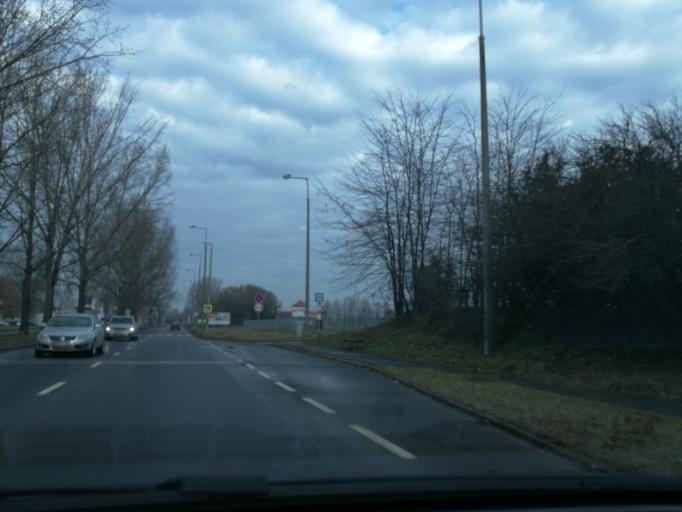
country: HU
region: Szabolcs-Szatmar-Bereg
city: Nyiregyhaza
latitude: 47.9584
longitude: 21.7439
